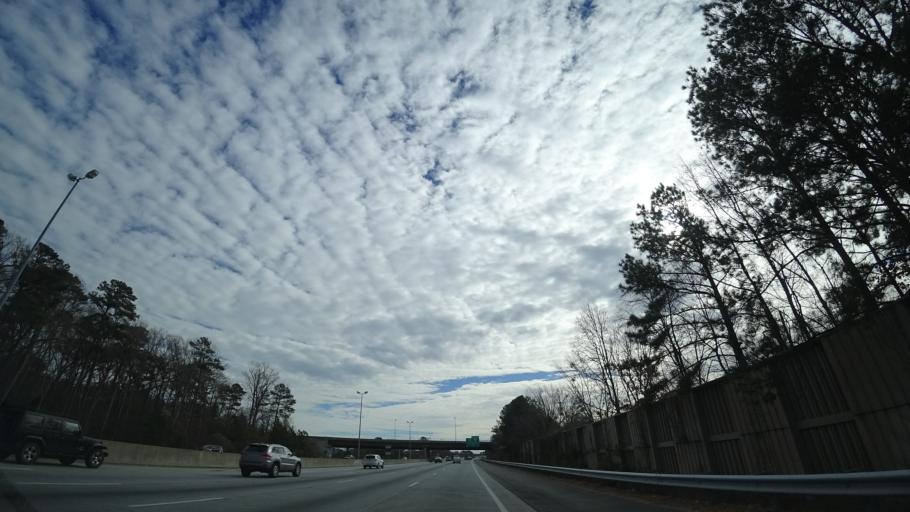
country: US
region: Virginia
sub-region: City of Hampton
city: Hampton
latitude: 37.0529
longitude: -76.4088
